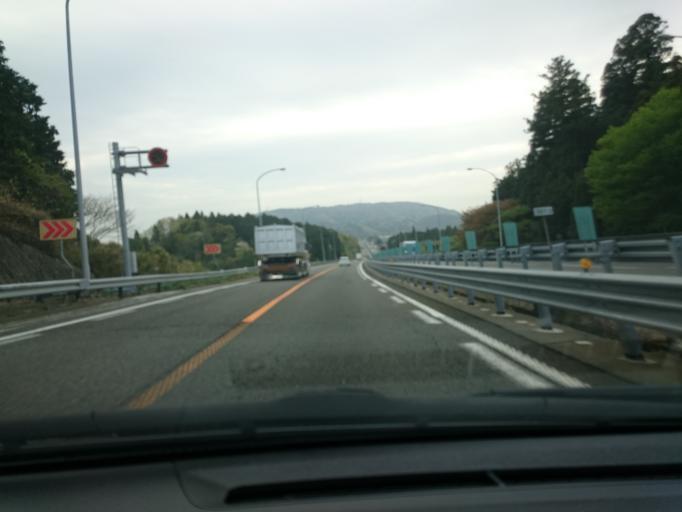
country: JP
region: Gifu
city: Tarui
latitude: 35.3554
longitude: 136.4516
